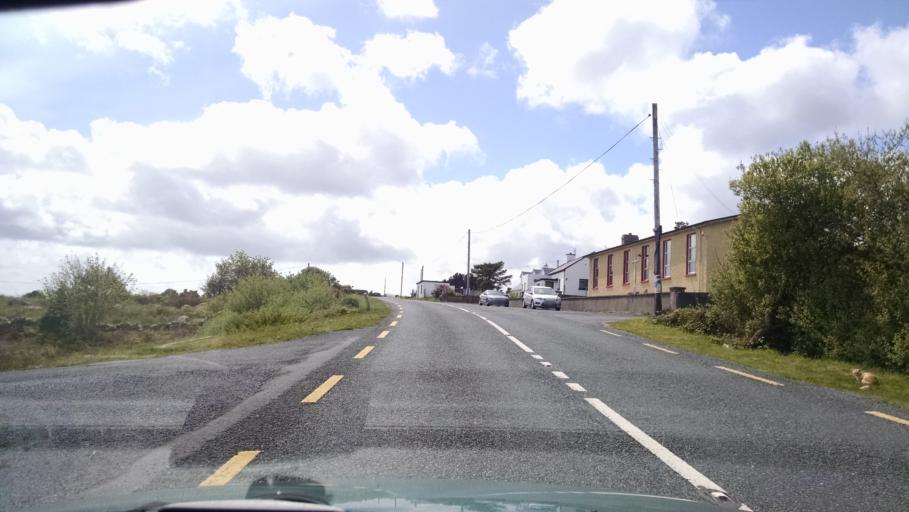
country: IE
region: Connaught
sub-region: County Galway
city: Clifden
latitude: 53.3671
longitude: -9.6896
